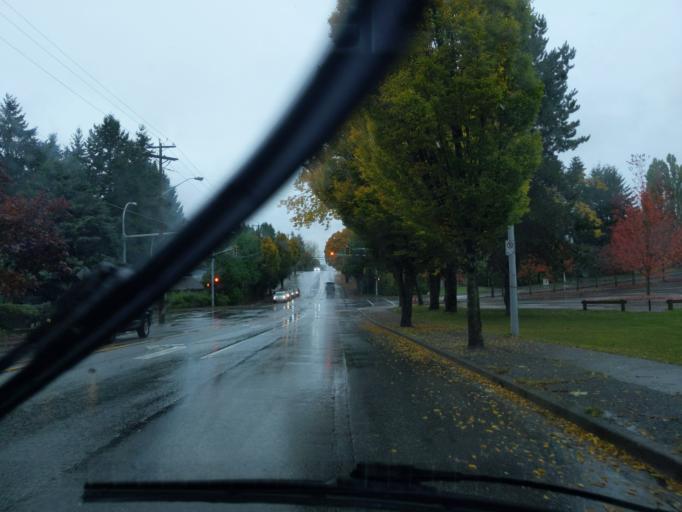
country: CA
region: British Columbia
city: New Westminster
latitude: 49.1917
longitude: -122.8625
